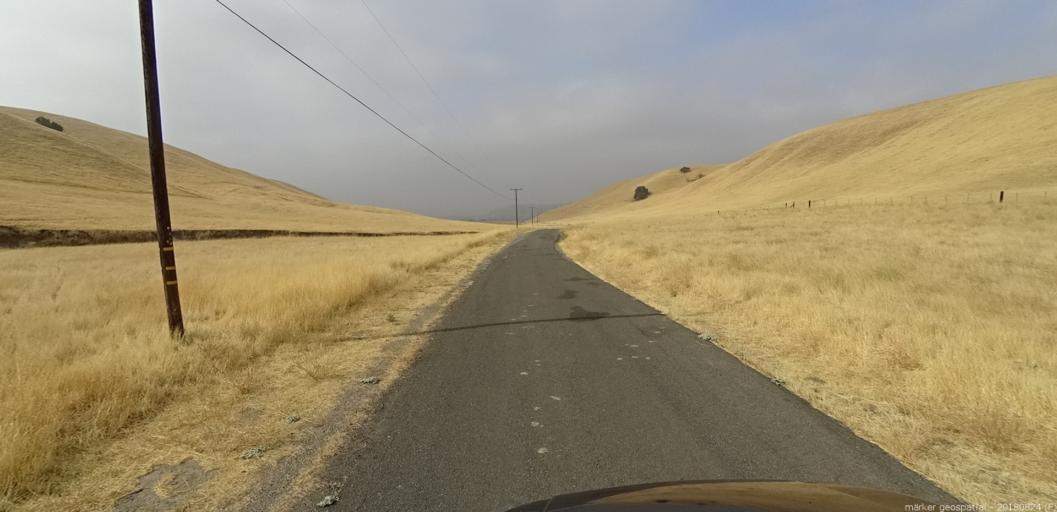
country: US
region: California
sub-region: San Luis Obispo County
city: San Miguel
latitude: 35.8782
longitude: -120.7896
